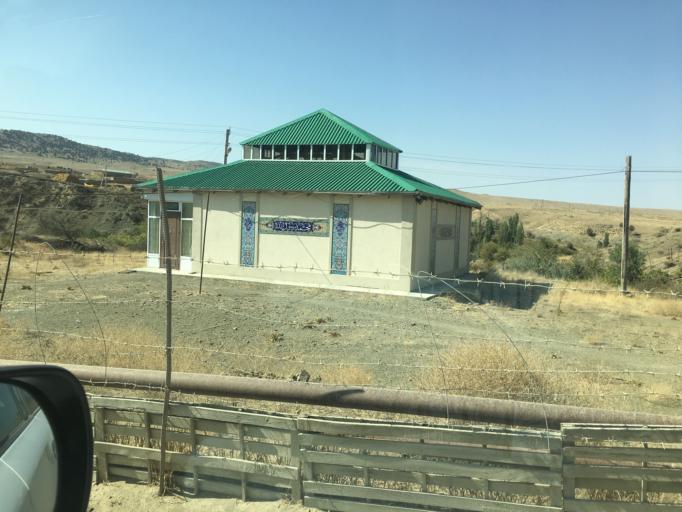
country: TM
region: Ahal
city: Baharly
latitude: 38.3870
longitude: 56.9549
